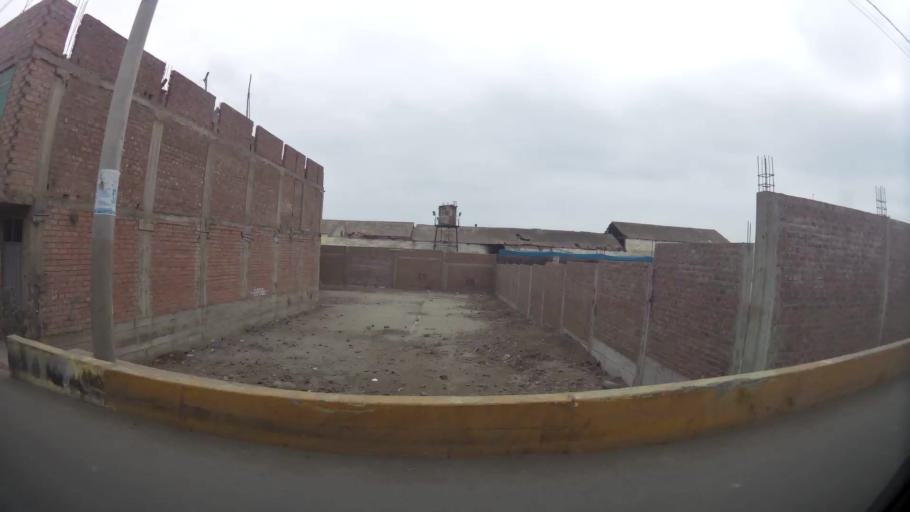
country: PE
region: Lima
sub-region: Provincia de Huaral
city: Huaral
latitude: -11.4929
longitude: -77.2002
